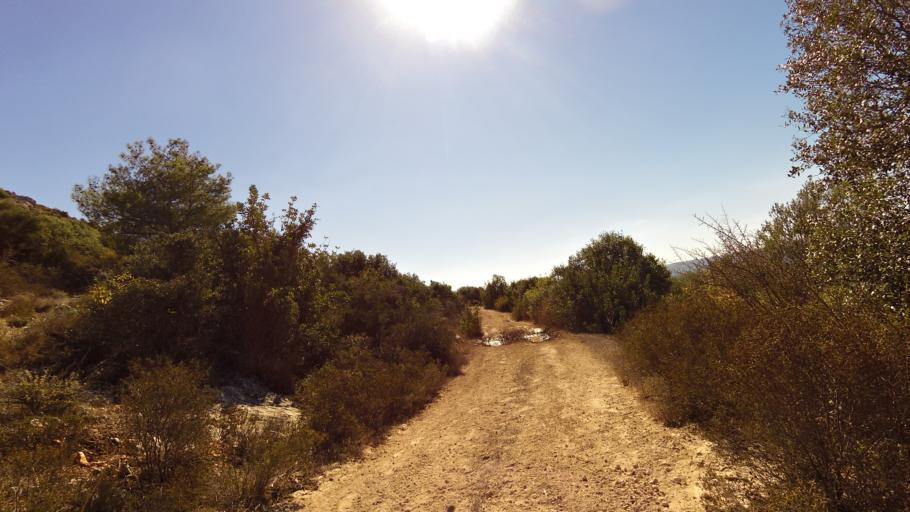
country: CY
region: Pafos
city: Polis
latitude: 35.0118
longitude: 32.4792
